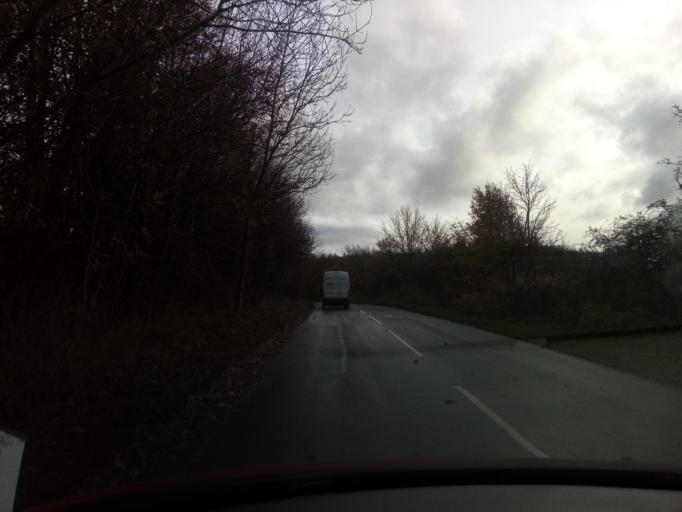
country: GB
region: England
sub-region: Northumberland
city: Birtley
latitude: 55.0563
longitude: -2.1908
